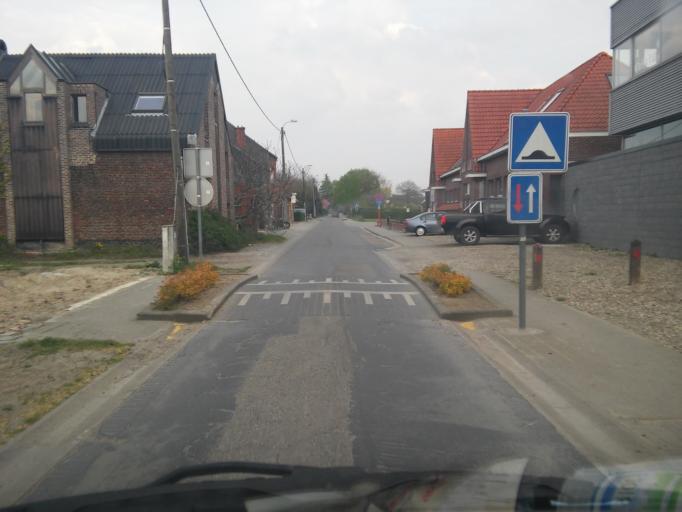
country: BE
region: Flanders
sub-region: Provincie Antwerpen
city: Mechelen
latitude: 51.0255
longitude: 4.4506
